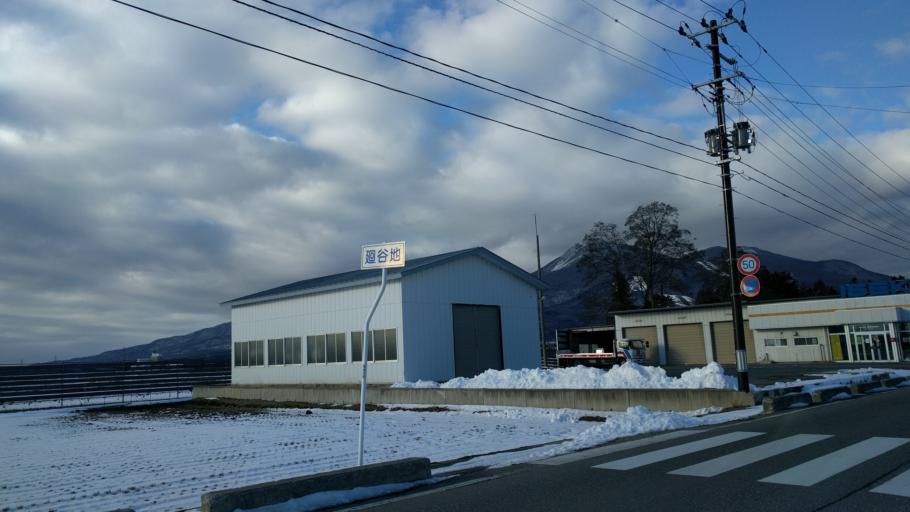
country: JP
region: Fukushima
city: Inawashiro
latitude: 37.5394
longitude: 140.1043
